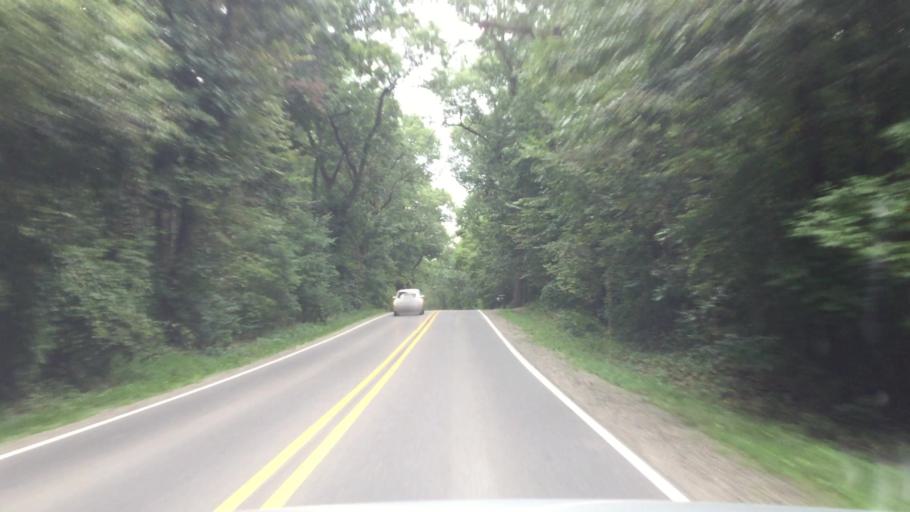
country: US
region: Michigan
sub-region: Livingston County
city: Whitmore Lake
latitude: 42.4619
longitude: -83.7866
